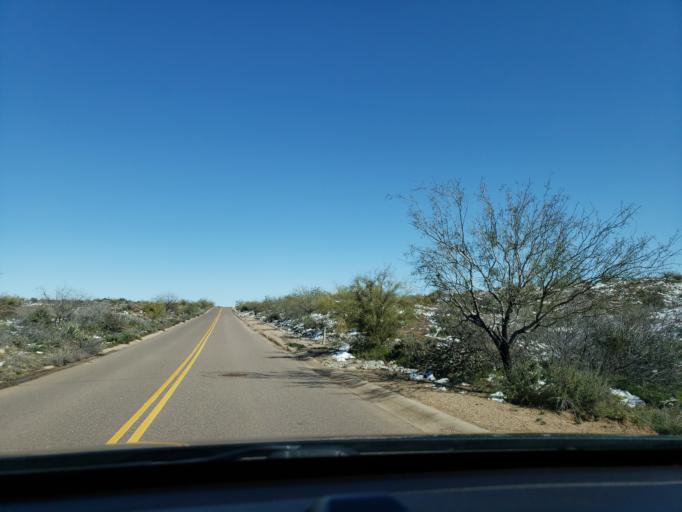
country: US
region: Arizona
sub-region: Maricopa County
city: Carefree
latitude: 33.7162
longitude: -111.8213
